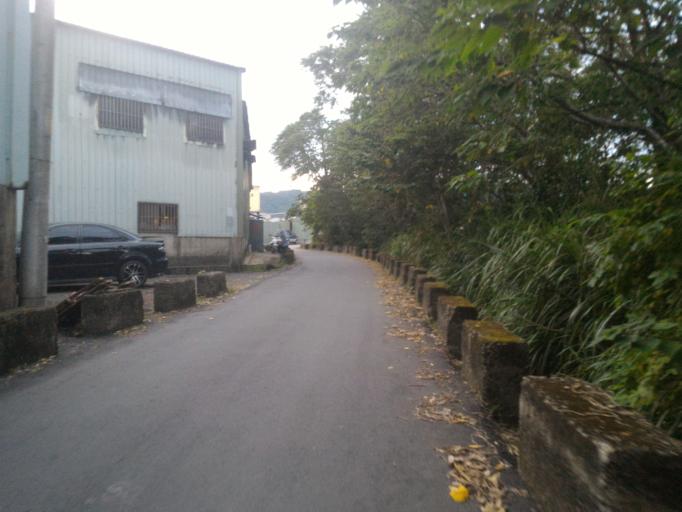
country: TW
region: Taiwan
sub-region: Taoyuan
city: Taoyuan
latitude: 24.9526
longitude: 121.3907
